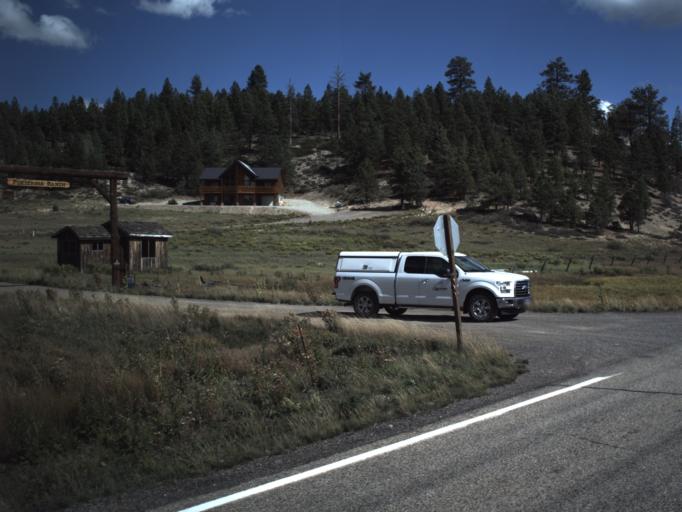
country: US
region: Utah
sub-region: Garfield County
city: Panguitch
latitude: 37.4927
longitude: -112.5738
